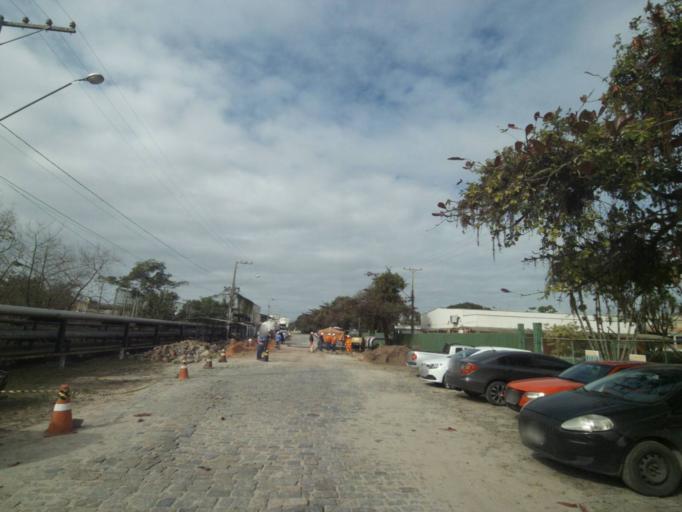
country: BR
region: Parana
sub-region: Paranagua
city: Paranagua
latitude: -25.5060
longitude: -48.5340
